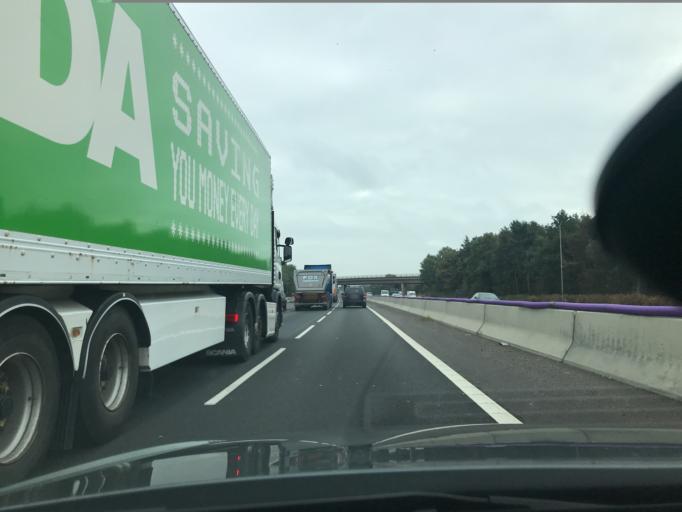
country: GB
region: England
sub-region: Cheshire East
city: Peover Superior
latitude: 53.2349
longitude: -2.3992
